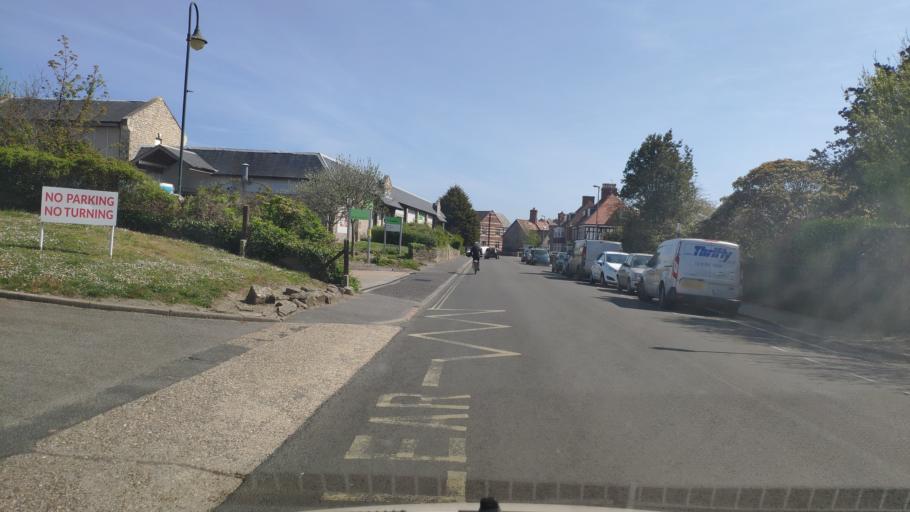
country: GB
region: England
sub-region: Dorset
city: Swanage
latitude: 50.6093
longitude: -1.9622
